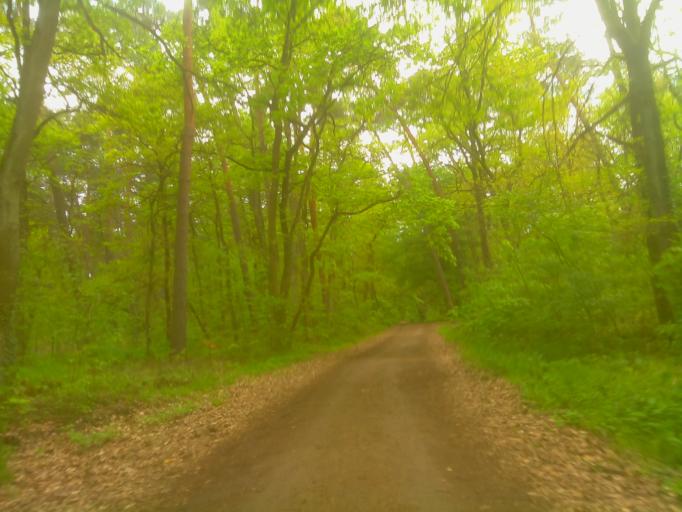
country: DE
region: Baden-Wuerttemberg
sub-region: Karlsruhe Region
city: Sandhausen
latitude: 49.3495
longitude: 8.6330
